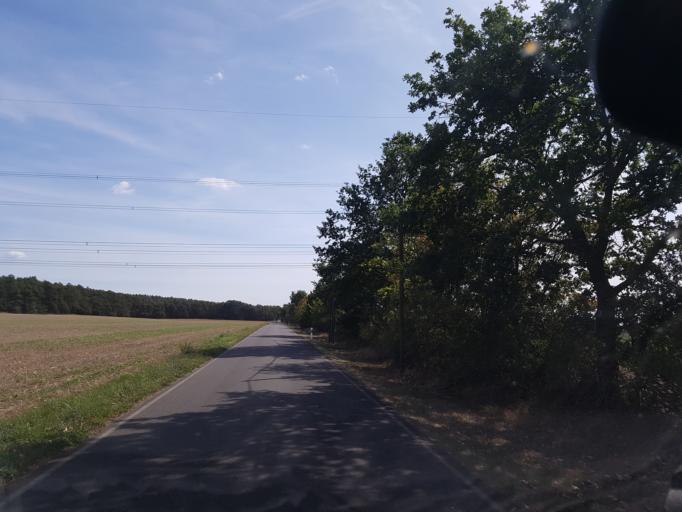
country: DE
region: Brandenburg
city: Luckau
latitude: 51.8619
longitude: 13.6505
